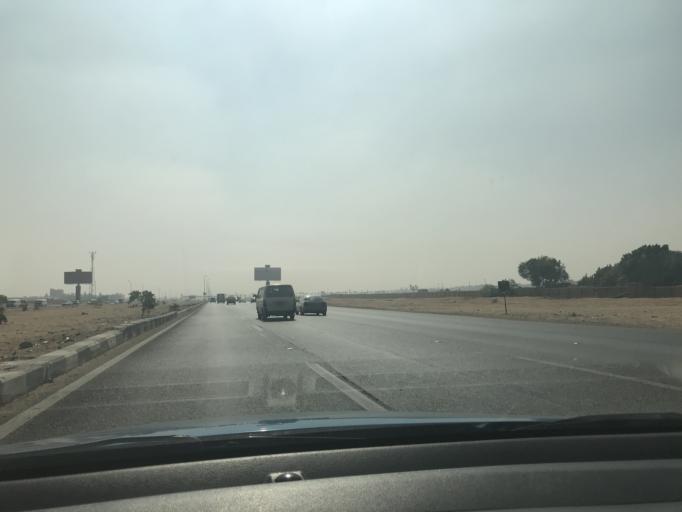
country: EG
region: Muhafazat al Qalyubiyah
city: Al Khankah
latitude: 30.1726
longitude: 31.5428
